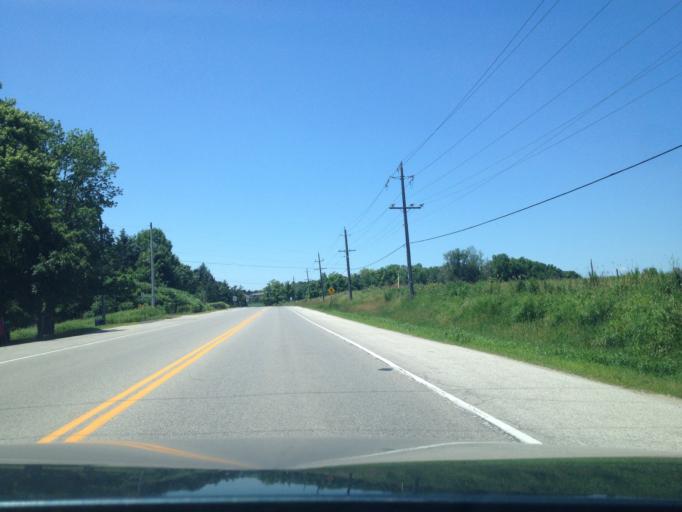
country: CA
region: Ontario
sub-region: Wellington County
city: Guelph
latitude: 43.6927
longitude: -80.4053
